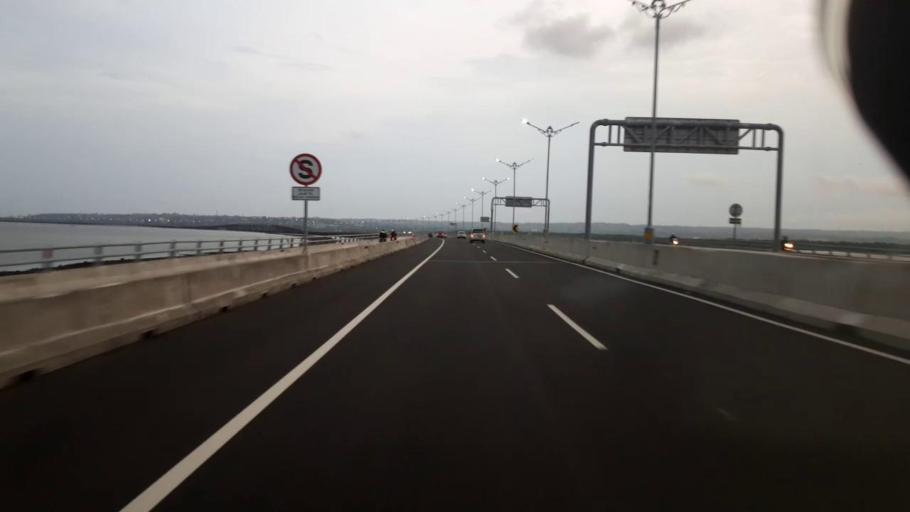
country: ID
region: Bali
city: Kelanabian
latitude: -8.7560
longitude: 115.1951
